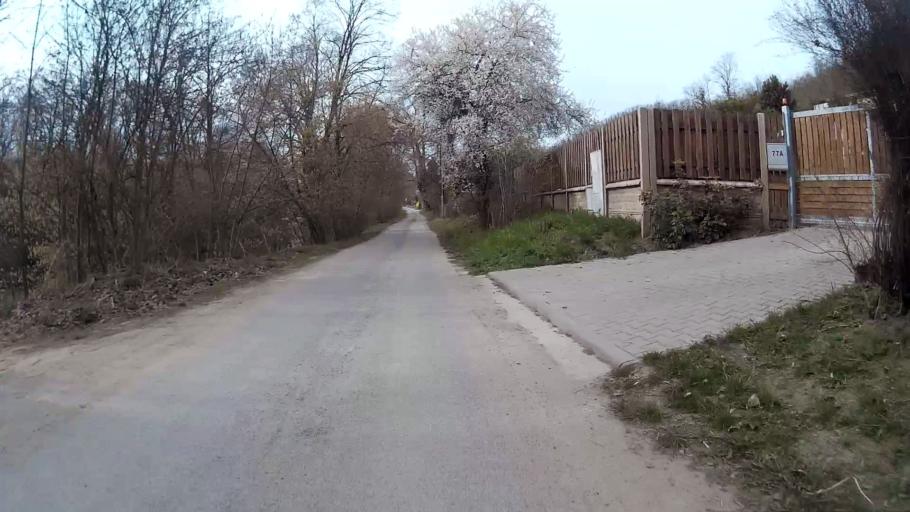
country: CZ
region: South Moravian
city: Dolni Kounice
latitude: 49.0644
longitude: 16.4784
